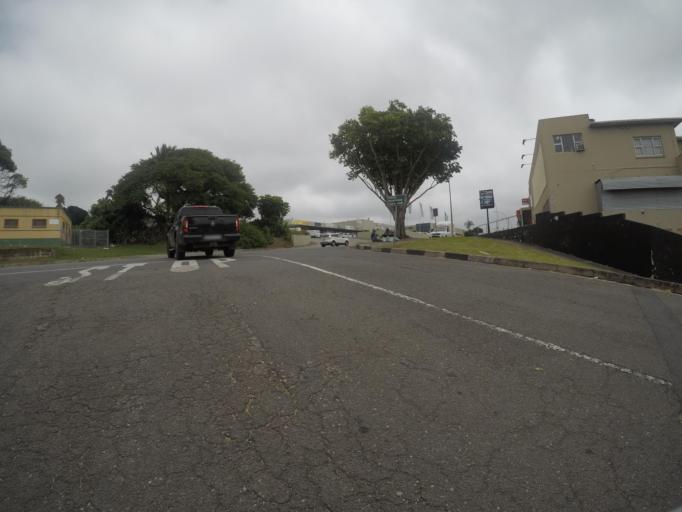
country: ZA
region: Eastern Cape
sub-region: Buffalo City Metropolitan Municipality
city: East London
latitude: -32.9872
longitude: 27.9203
